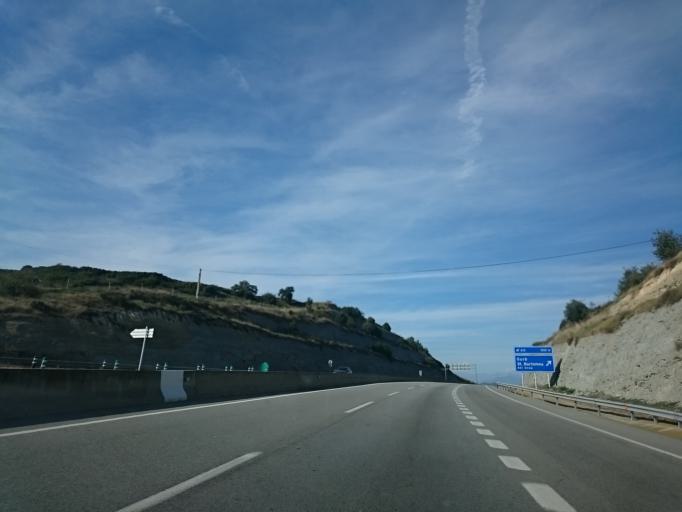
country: ES
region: Catalonia
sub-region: Provincia de Barcelona
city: Vic
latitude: 41.9288
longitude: 2.2304
